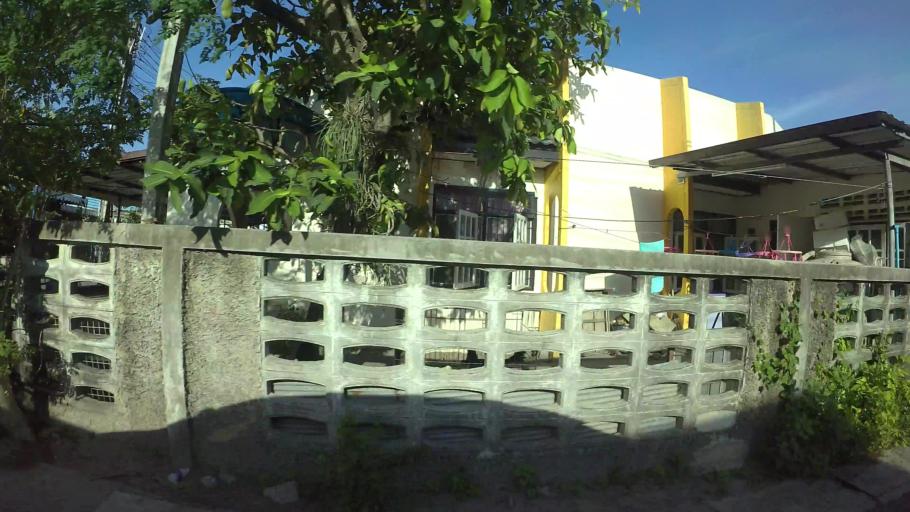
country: TH
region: Rayong
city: Rayong
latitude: 12.6910
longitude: 101.2792
